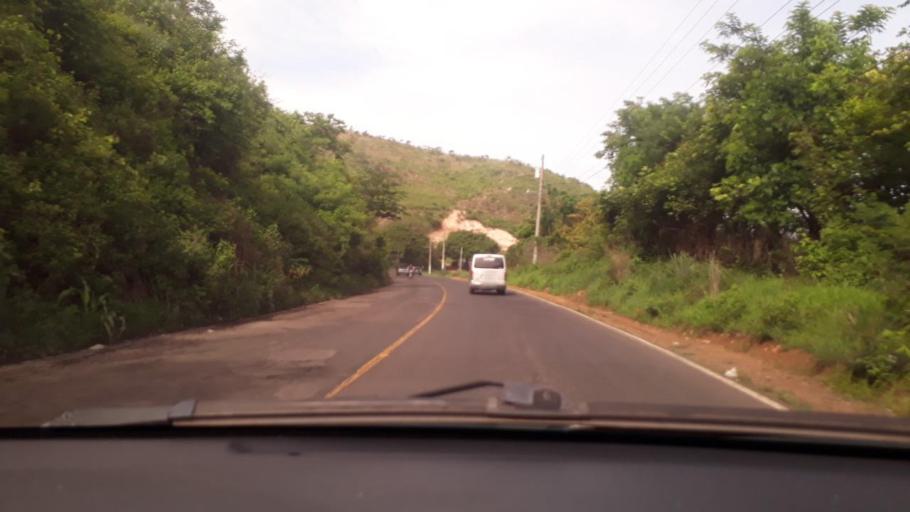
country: GT
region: Jutiapa
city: Quesada
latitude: 14.2758
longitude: -89.9948
